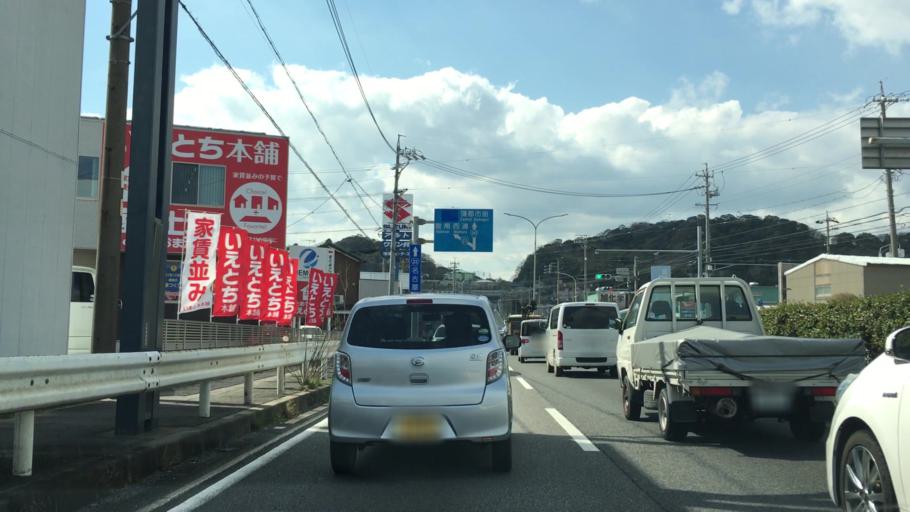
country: JP
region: Aichi
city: Gamagori
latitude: 34.8112
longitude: 137.2722
